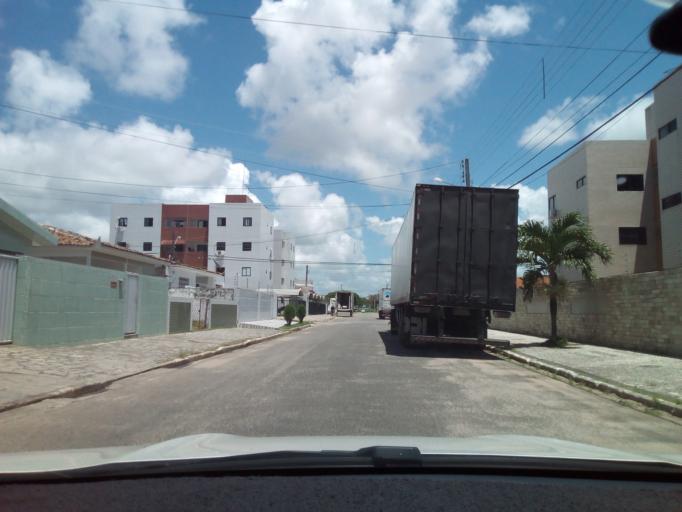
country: BR
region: Paraiba
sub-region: Joao Pessoa
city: Joao Pessoa
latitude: -7.1660
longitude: -34.8687
